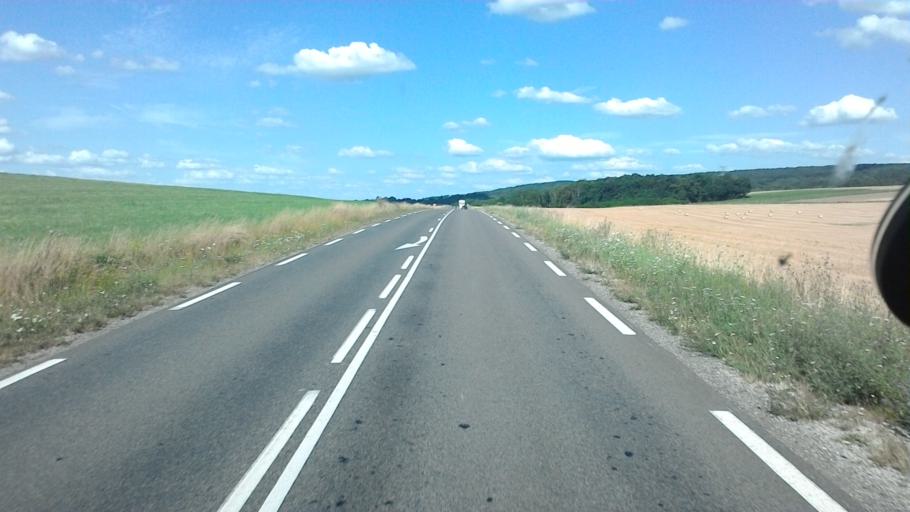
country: FR
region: Franche-Comte
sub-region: Departement de la Haute-Saone
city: Gy
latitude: 47.3841
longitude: 5.7799
